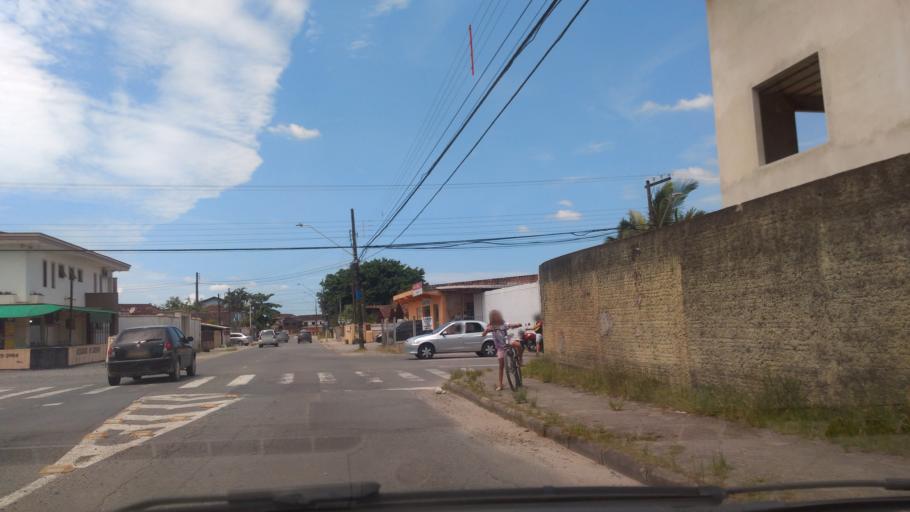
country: BR
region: Santa Catarina
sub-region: Joinville
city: Joinville
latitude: -26.3227
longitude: -48.8153
